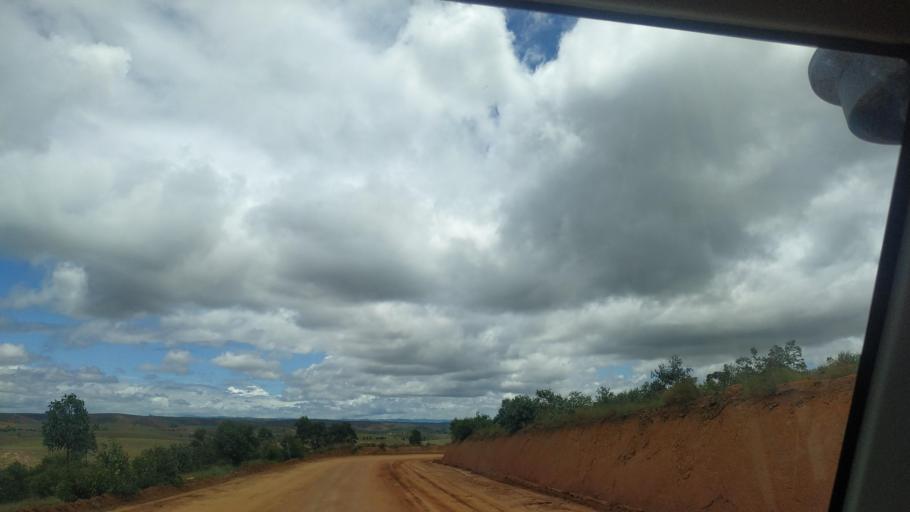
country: MG
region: Alaotra Mangoro
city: Ambatondrazaka
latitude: -17.9759
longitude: 48.2572
